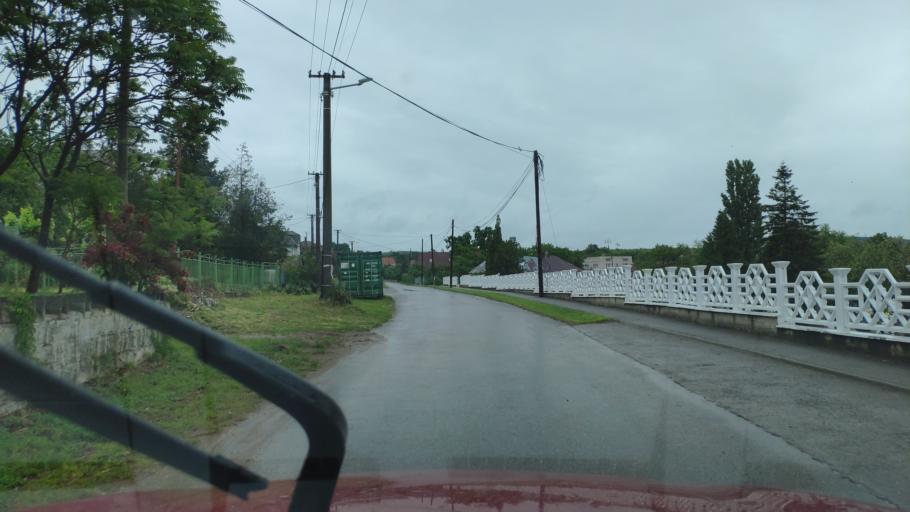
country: HU
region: Borsod-Abauj-Zemplen
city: Satoraljaujhely
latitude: 48.4240
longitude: 21.7151
